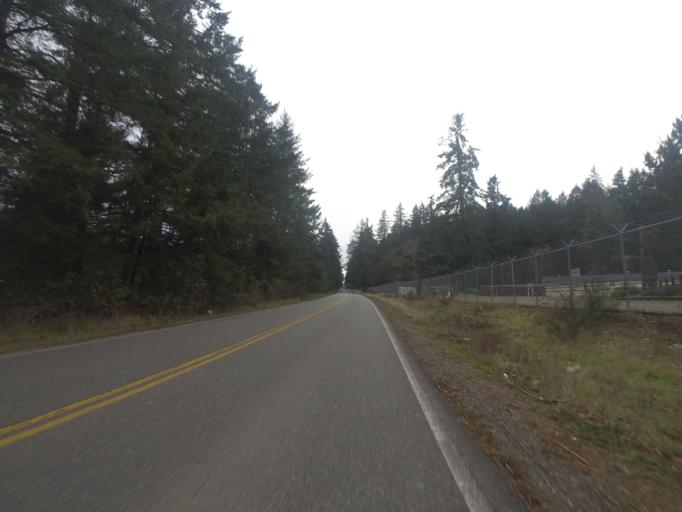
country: US
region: Washington
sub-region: Pierce County
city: McChord Air Force Base
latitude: 47.1213
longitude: -122.5114
